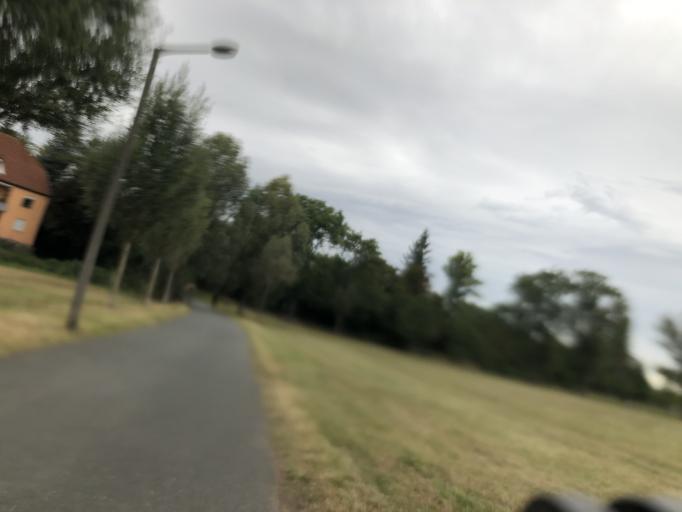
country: DE
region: Bavaria
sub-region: Regierungsbezirk Mittelfranken
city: Furth
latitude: 49.4840
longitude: 10.9802
